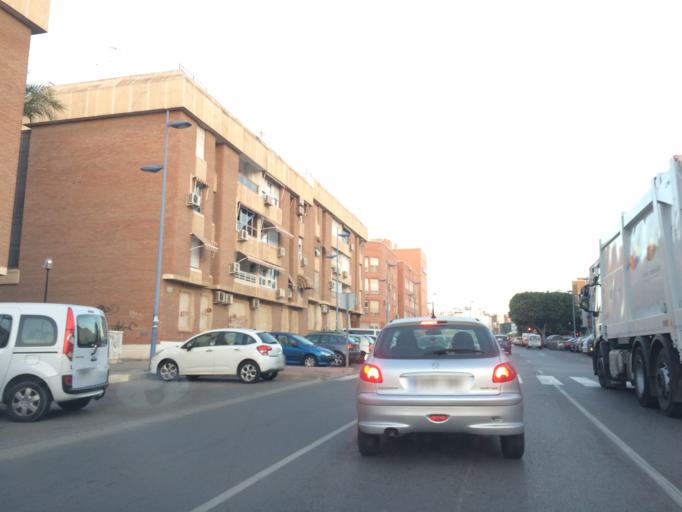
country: ES
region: Andalusia
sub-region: Provincia de Almeria
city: Almeria
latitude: 36.8421
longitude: -2.4499
